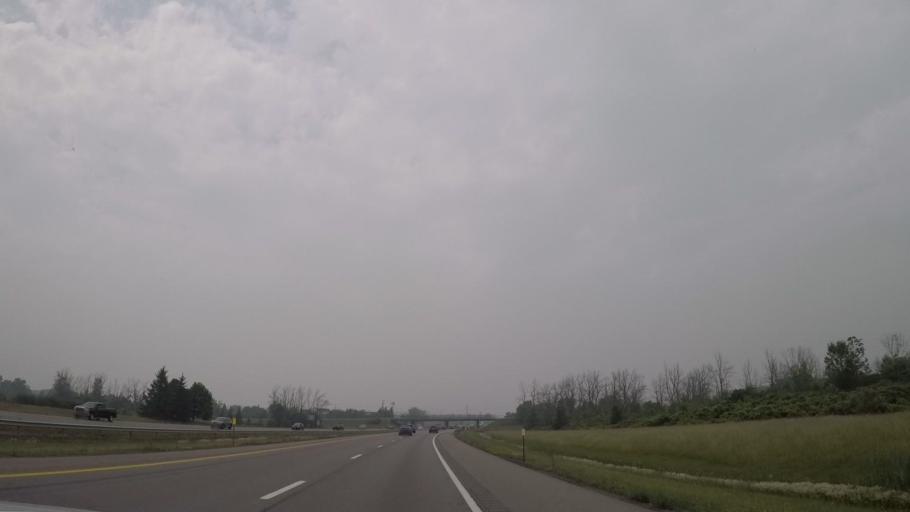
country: US
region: New York
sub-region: Erie County
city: Grandyle Village
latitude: 43.0460
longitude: -78.9899
